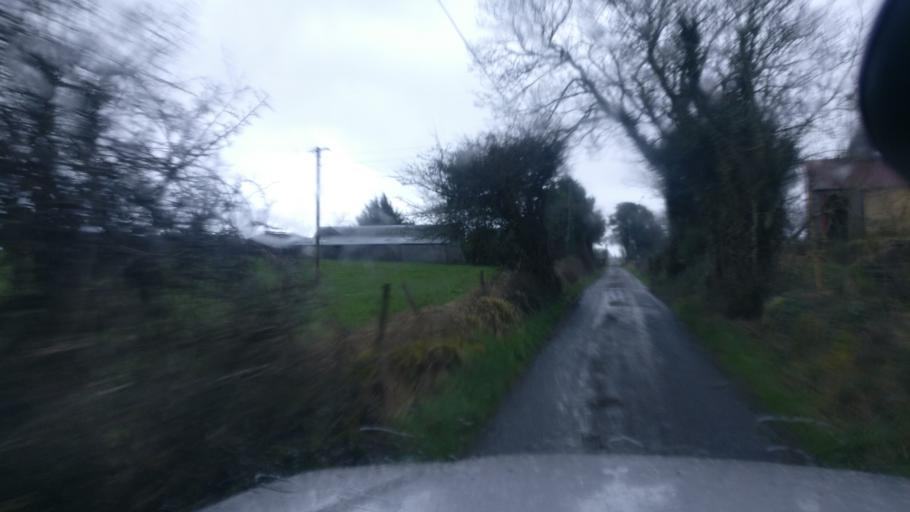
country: IE
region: Connaught
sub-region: County Galway
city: Loughrea
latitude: 53.2403
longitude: -8.4230
